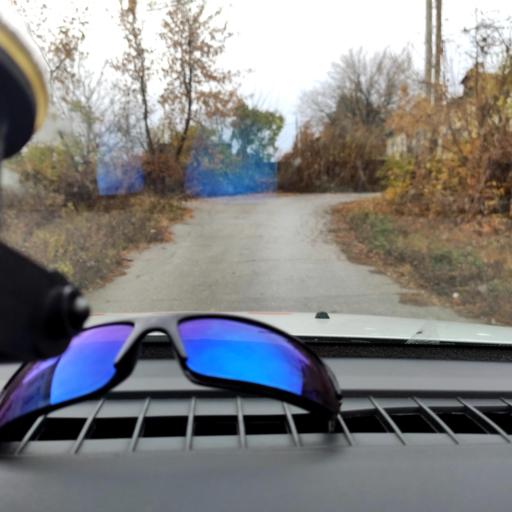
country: RU
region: Samara
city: Samara
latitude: 53.1716
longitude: 50.1745
